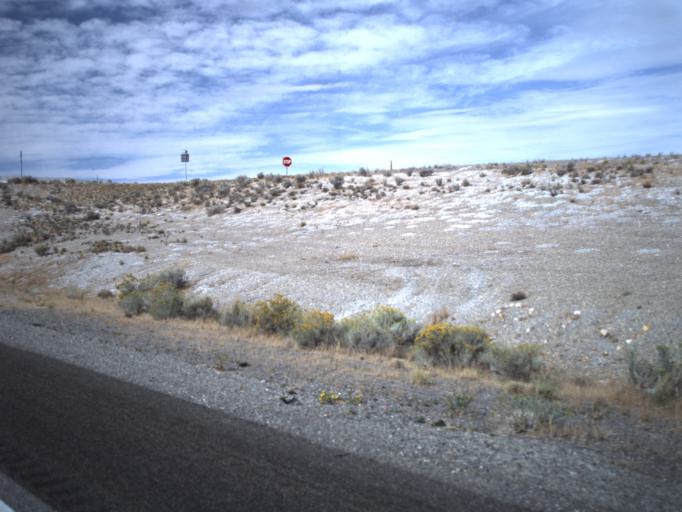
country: US
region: Utah
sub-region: Tooele County
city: Grantsville
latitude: 40.7694
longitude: -112.9837
